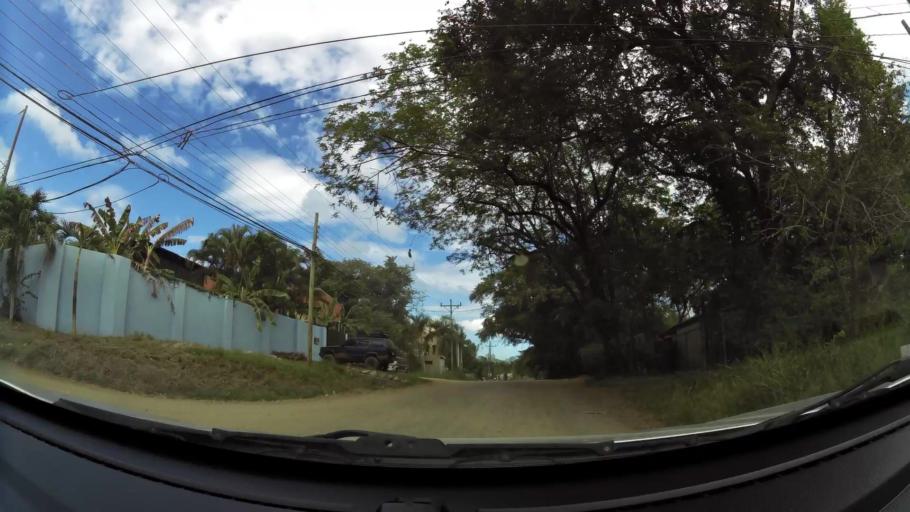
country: CR
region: Guanacaste
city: Santa Cruz
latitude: 10.2883
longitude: -85.8490
